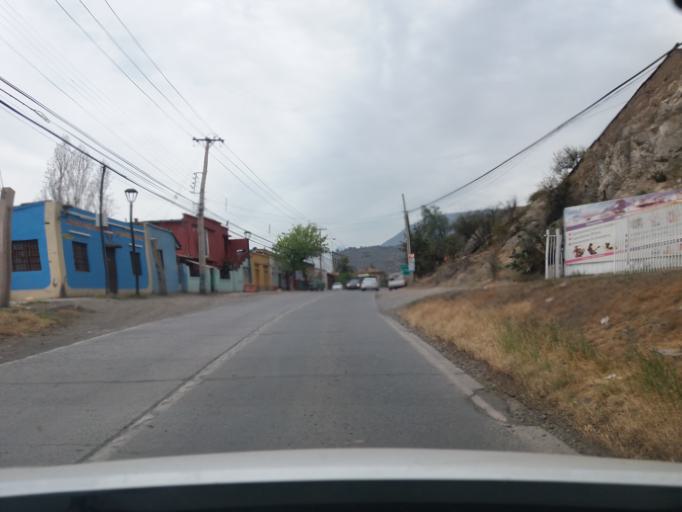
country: CL
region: Valparaiso
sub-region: Provincia de Los Andes
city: Los Andes
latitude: -32.8354
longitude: -70.5849
